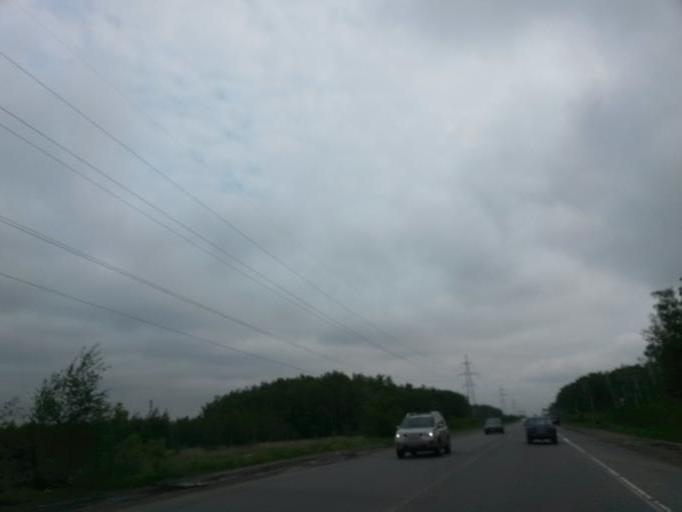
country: RU
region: Moskovskaya
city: Shcherbinka
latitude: 55.4935
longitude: 37.5844
